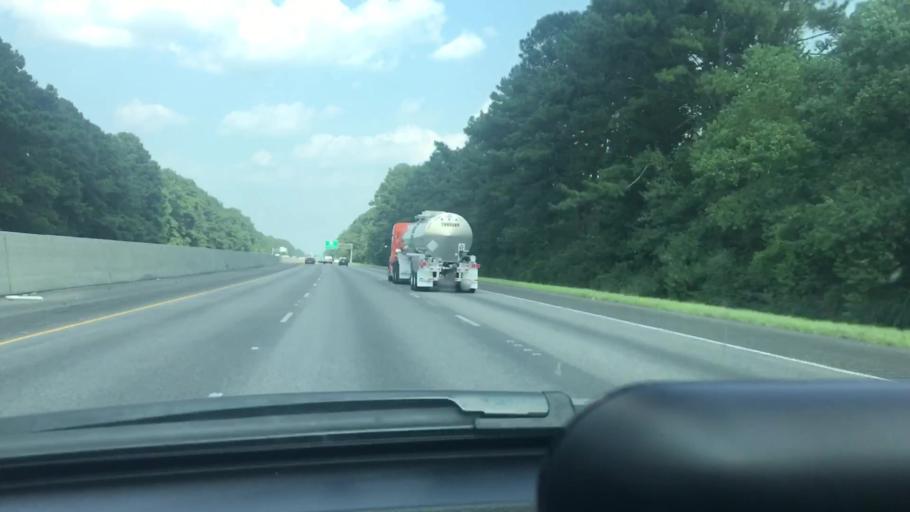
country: US
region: Louisiana
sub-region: Livingston Parish
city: Walker
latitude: 30.4668
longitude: -90.8873
